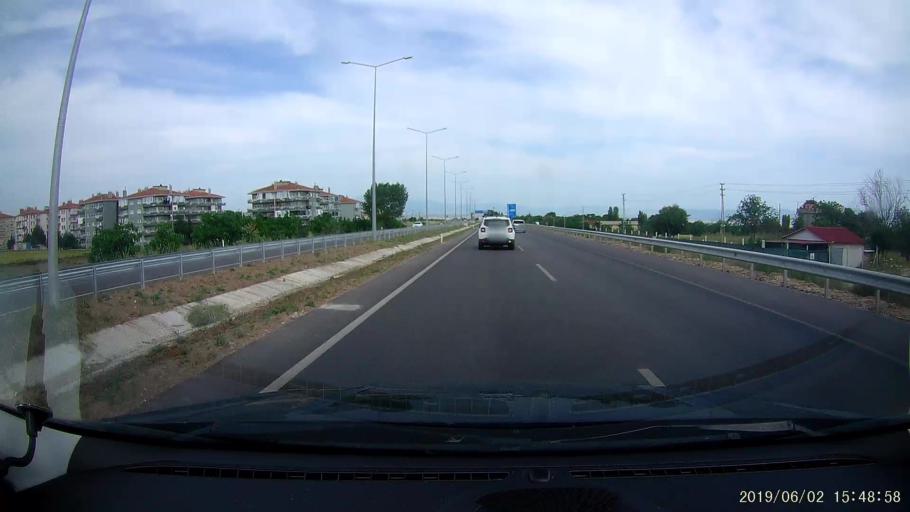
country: TR
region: Amasya
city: Merzifon
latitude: 40.8595
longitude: 35.4524
